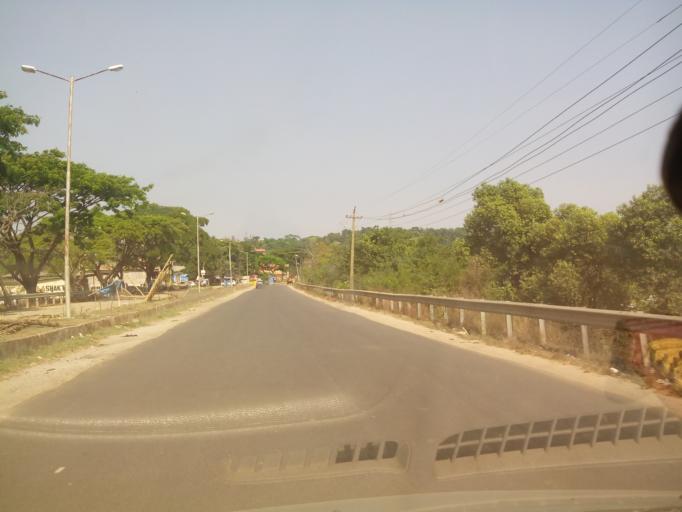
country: IN
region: Karnataka
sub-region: Hassan
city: Sakleshpur
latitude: 12.9448
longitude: 75.7951
